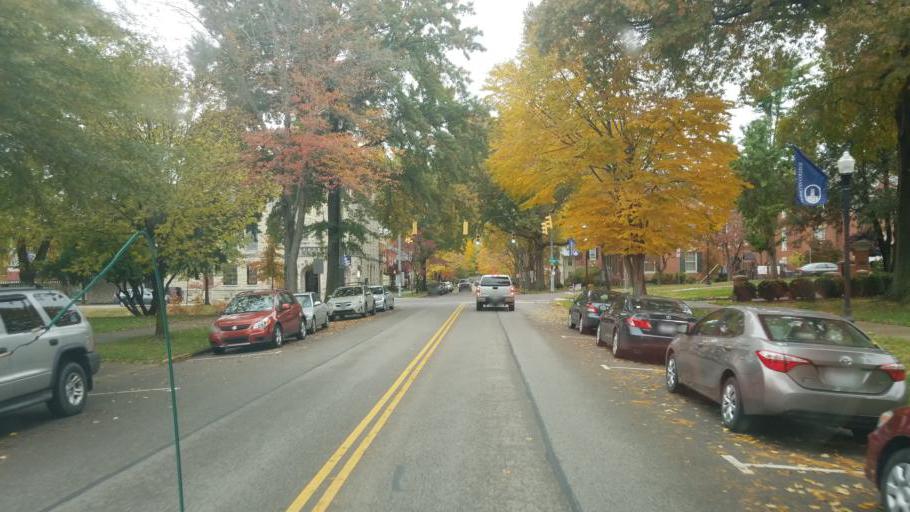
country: US
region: Ohio
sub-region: Washington County
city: Marietta
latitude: 39.4166
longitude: -81.4515
